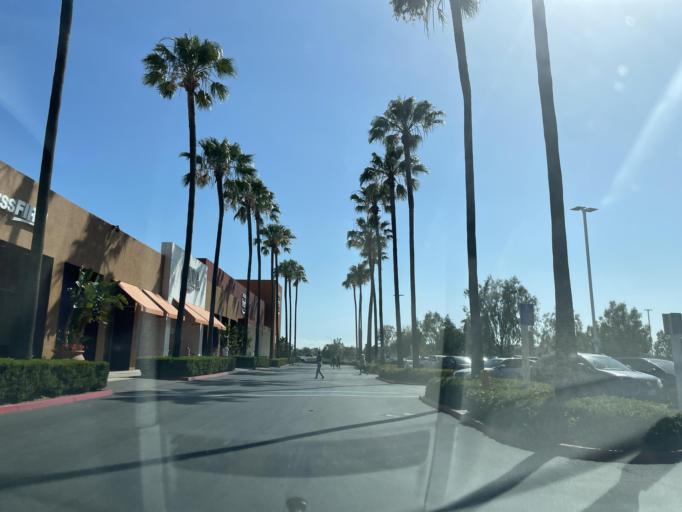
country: US
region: California
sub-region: Orange County
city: Tustin
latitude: 33.7207
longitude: -117.7918
